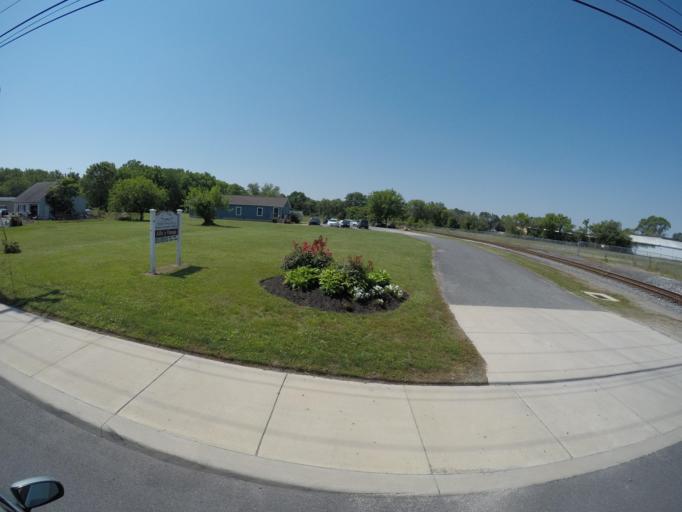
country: US
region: Delaware
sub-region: Sussex County
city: Georgetown
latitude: 38.6905
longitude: -75.3780
